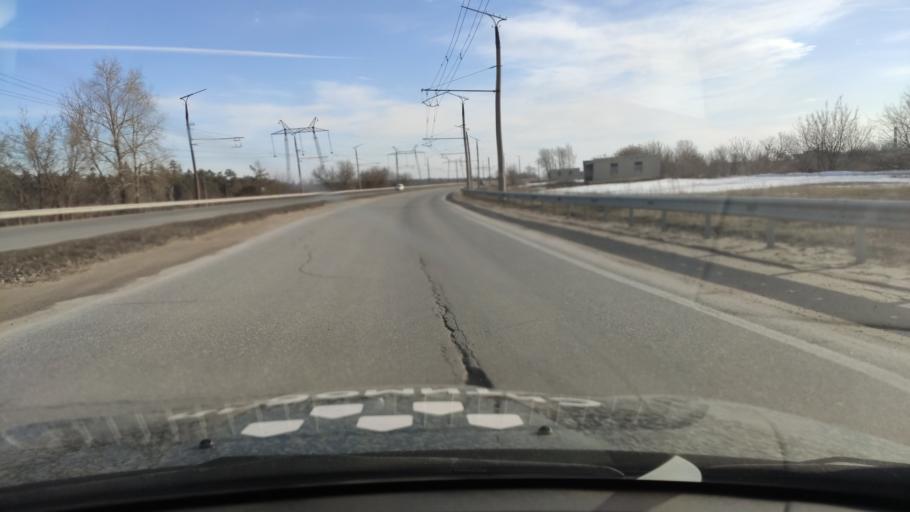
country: RU
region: Samara
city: Zhigulevsk
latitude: 53.5474
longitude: 49.5892
